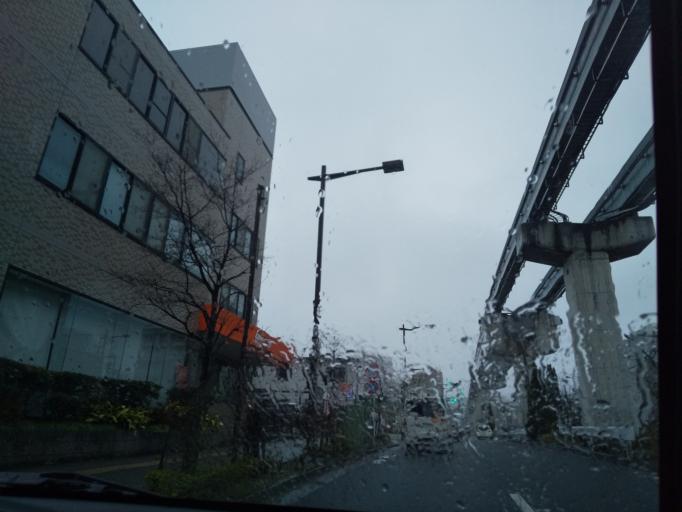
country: JP
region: Tokyo
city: Hino
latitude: 35.6911
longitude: 139.4099
